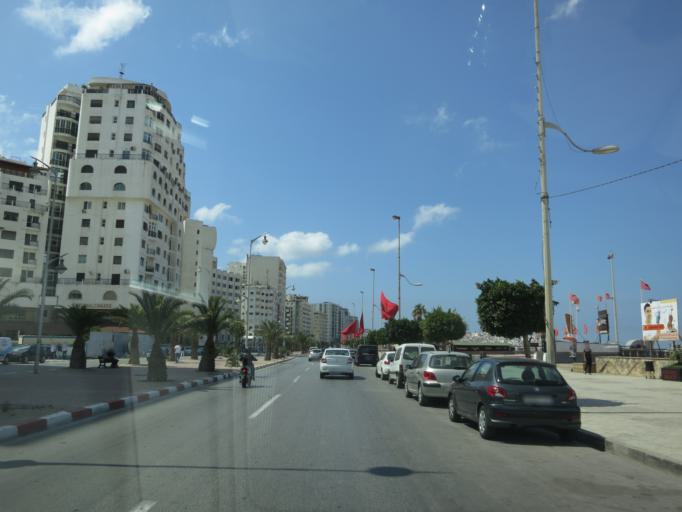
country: MA
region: Tanger-Tetouan
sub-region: Tanger-Assilah
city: Tangier
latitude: 35.7765
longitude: -5.7958
